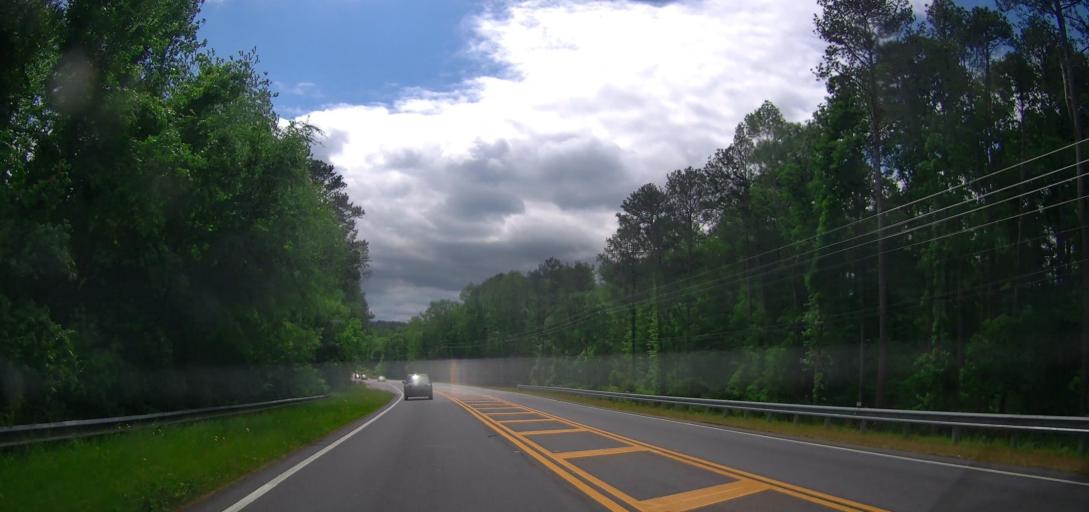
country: US
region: Georgia
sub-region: Rockdale County
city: Conyers
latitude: 33.6335
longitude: -84.0312
